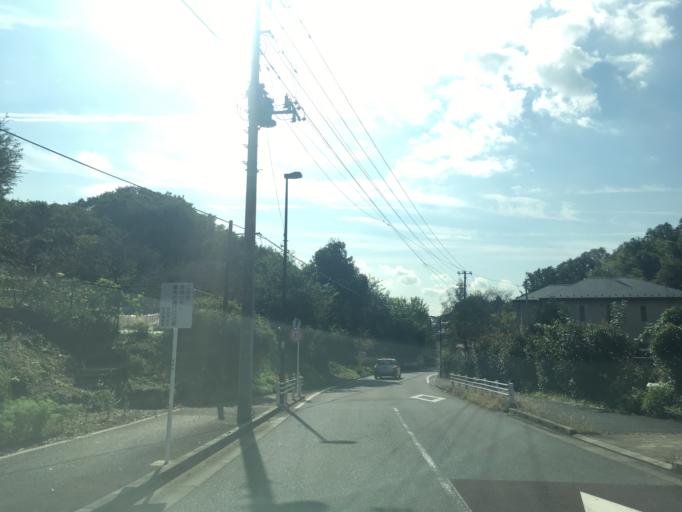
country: JP
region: Tokyo
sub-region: Machida-shi
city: Machida
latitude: 35.6000
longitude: 139.4088
